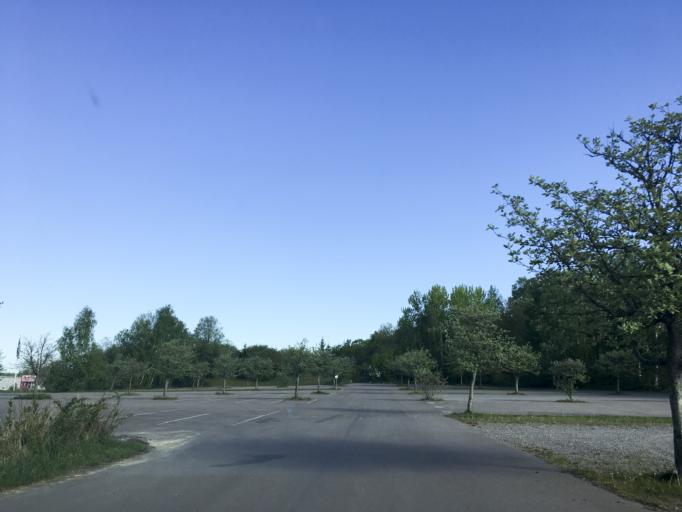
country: SE
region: Soedermanland
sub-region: Eskilstuna Kommun
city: Eskilstuna
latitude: 59.3725
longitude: 16.4748
